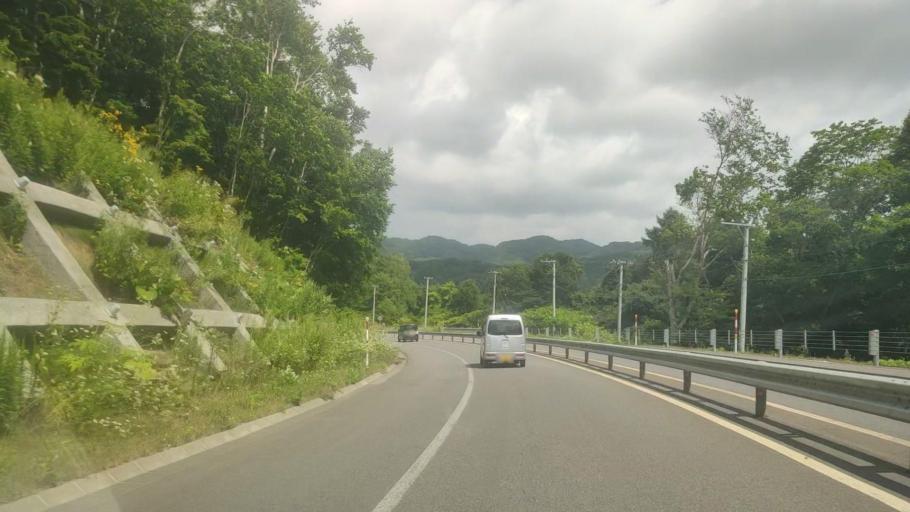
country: JP
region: Hokkaido
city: Niseko Town
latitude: 42.5978
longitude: 140.5796
